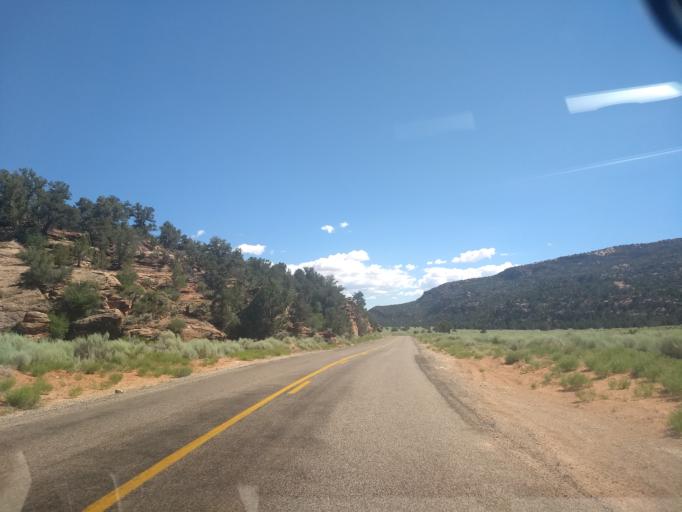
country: US
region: Utah
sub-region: Washington County
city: Hildale
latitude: 36.9865
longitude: -112.8682
